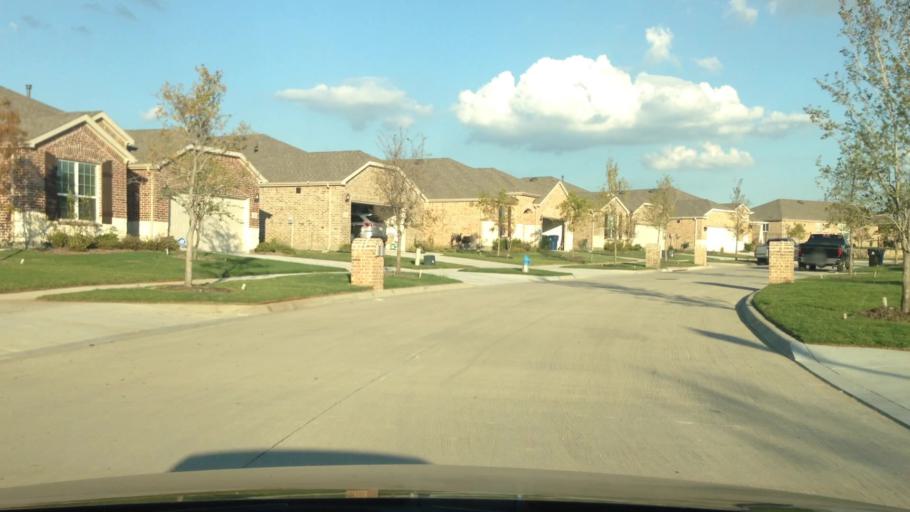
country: US
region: Texas
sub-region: Denton County
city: Little Elm
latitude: 33.1462
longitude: -96.9085
